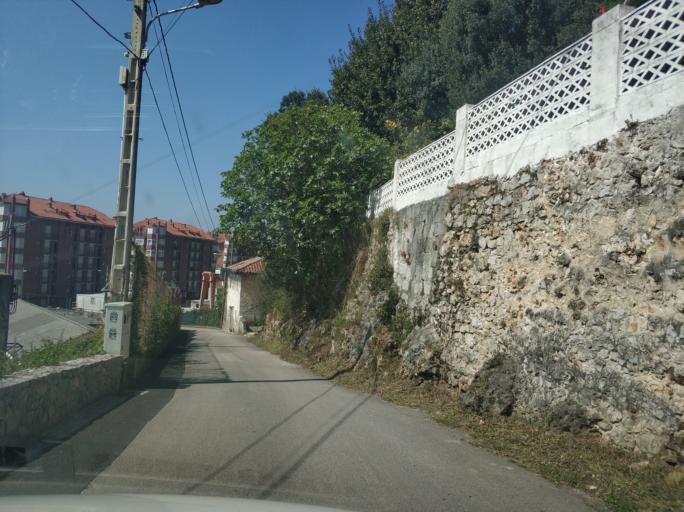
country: ES
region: Cantabria
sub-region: Provincia de Cantabria
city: Santona
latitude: 43.4403
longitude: -3.4475
